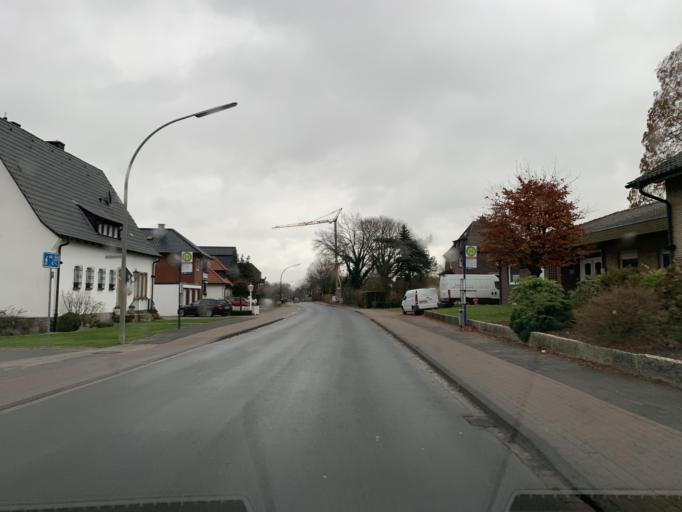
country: DE
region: North Rhine-Westphalia
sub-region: Regierungsbezirk Munster
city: Steinfurt
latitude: 52.1236
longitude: 7.4060
